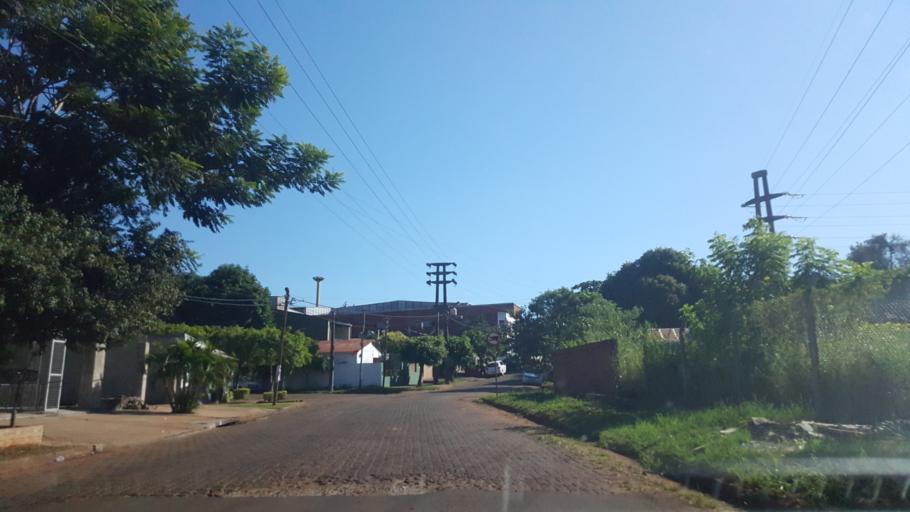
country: AR
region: Misiones
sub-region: Departamento de Capital
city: Posadas
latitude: -27.4061
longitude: -55.9016
